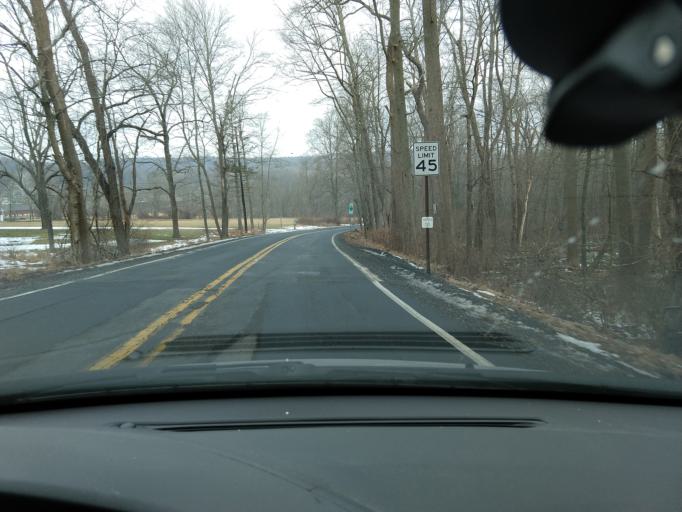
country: US
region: Pennsylvania
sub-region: Berks County
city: Birdsboro
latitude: 40.2010
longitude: -75.7723
